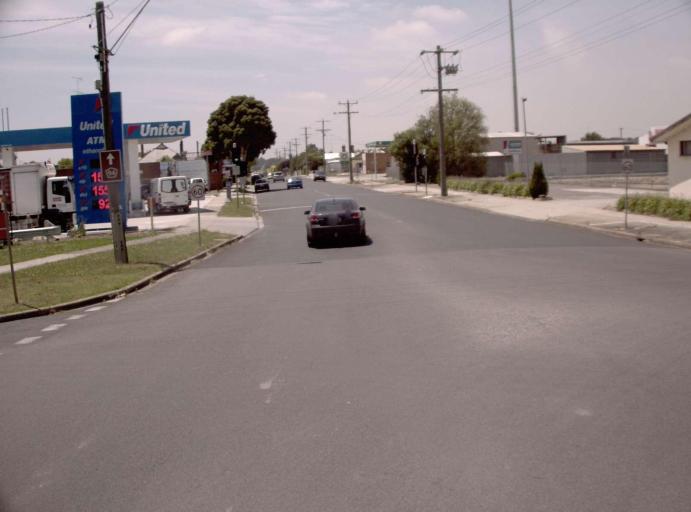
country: AU
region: Victoria
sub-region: Latrobe
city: Traralgon
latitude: -38.2005
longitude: 146.5347
